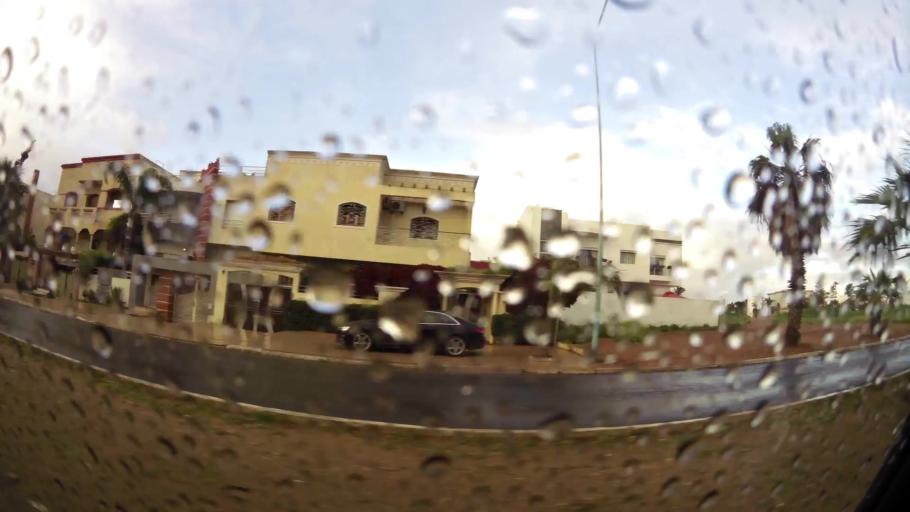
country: MA
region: Doukkala-Abda
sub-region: El-Jadida
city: El Jadida
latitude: 33.2438
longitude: -8.5130
